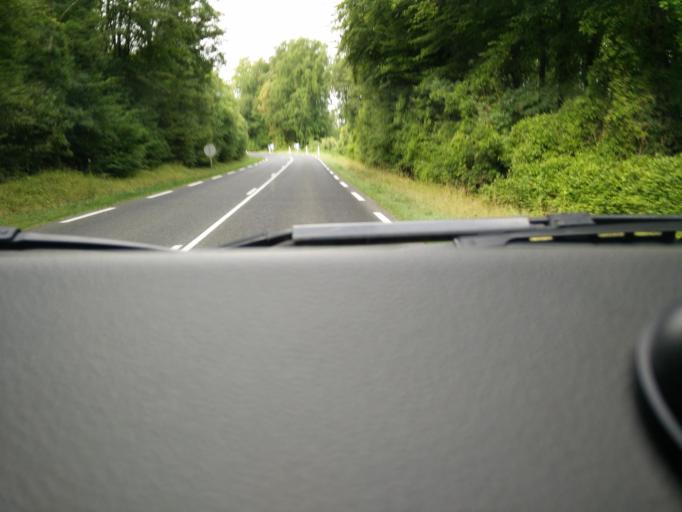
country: FR
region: Lorraine
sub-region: Departement de Meurthe-et-Moselle
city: Montauville
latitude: 48.9001
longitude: 5.9963
